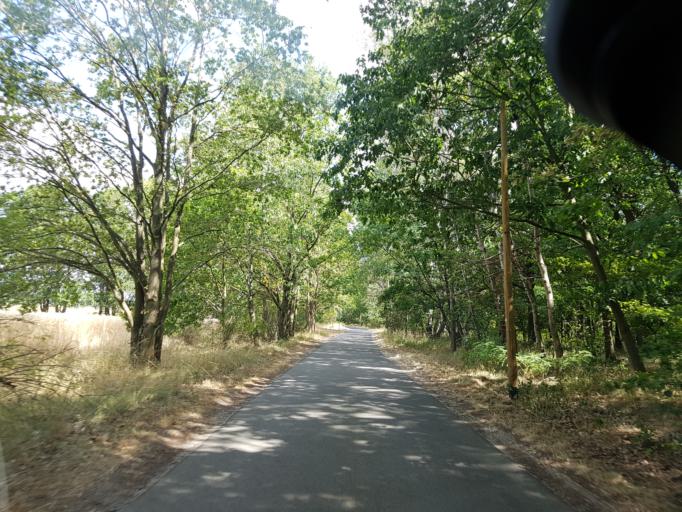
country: DE
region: Brandenburg
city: Cottbus
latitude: 51.6917
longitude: 14.3121
